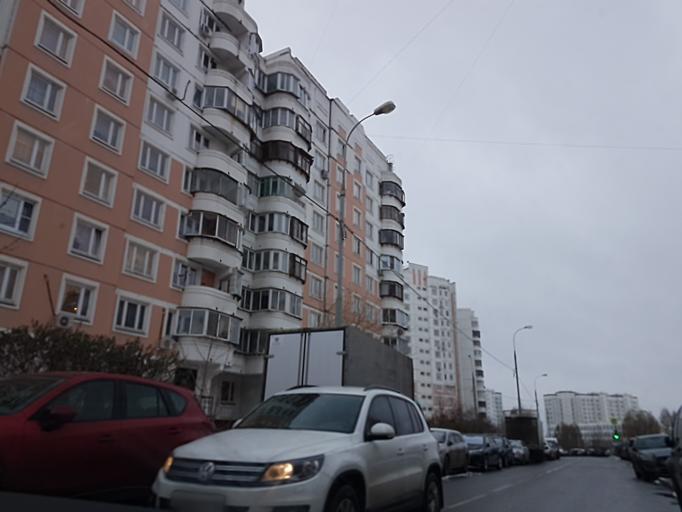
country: RU
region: Moskovskaya
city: Pavshino
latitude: 55.8313
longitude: 37.3507
